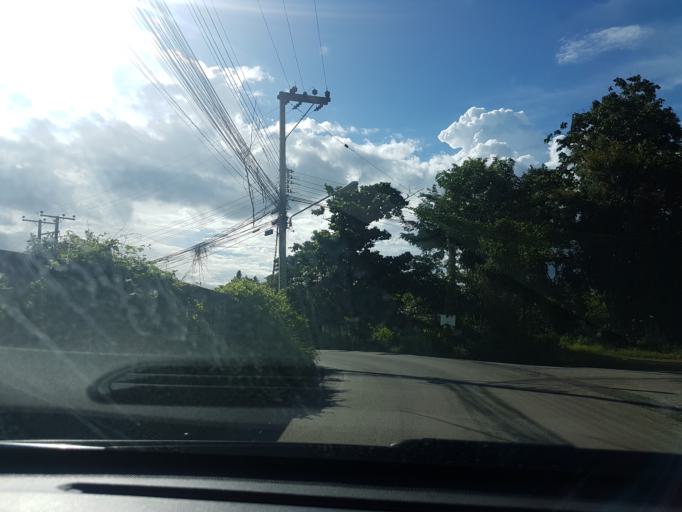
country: TH
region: Lampang
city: Ko Kha
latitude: 18.2332
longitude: 99.4263
